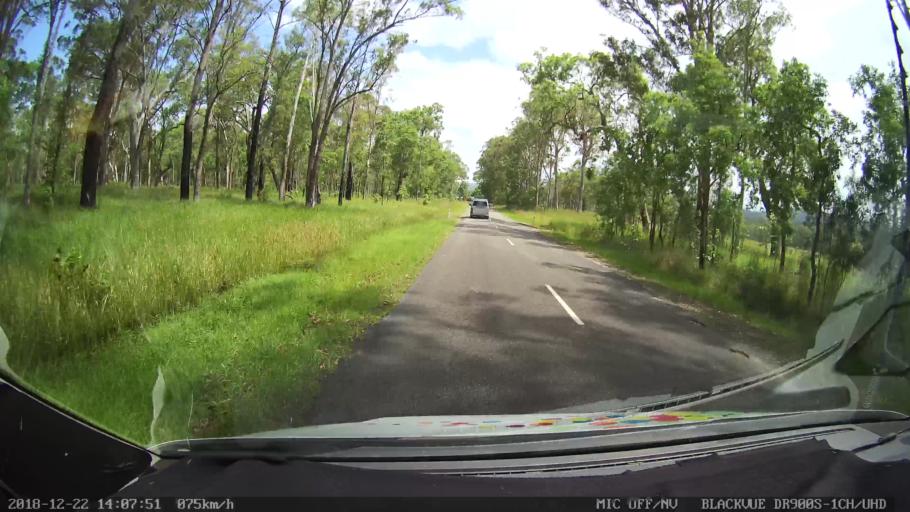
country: AU
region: New South Wales
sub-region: Clarence Valley
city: Coutts Crossing
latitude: -29.9719
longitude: 152.7264
